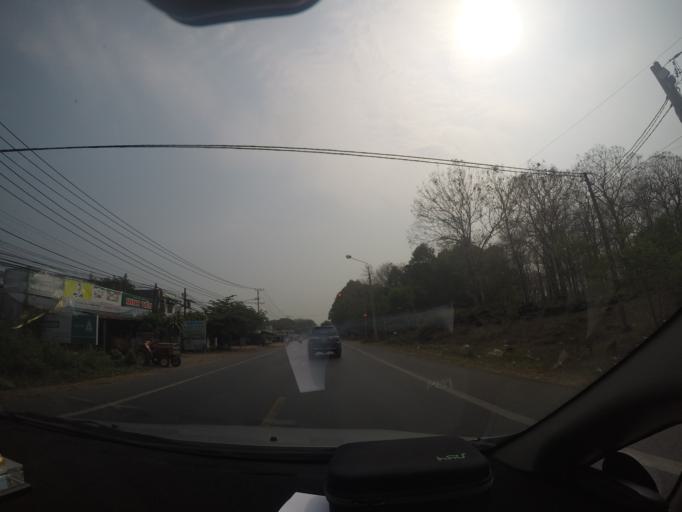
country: VN
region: Dong Nai
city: Tan Phu
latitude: 11.2382
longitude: 107.3900
